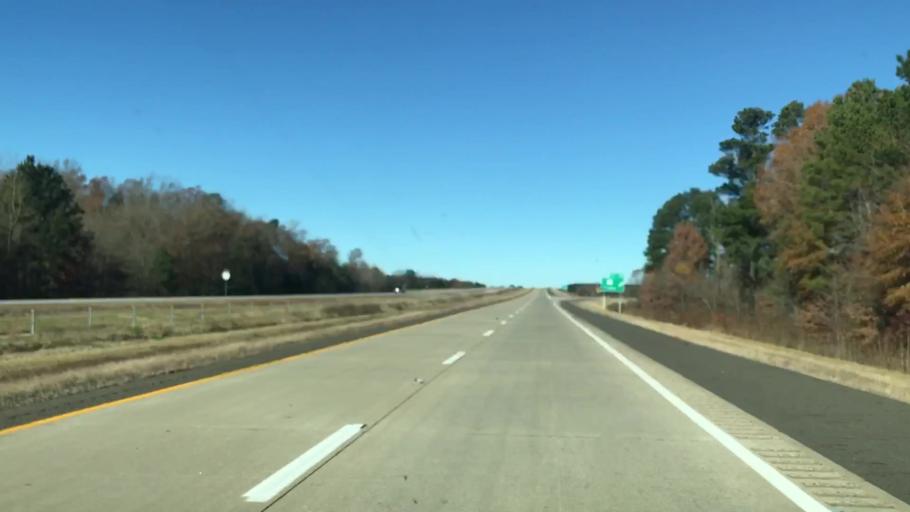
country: US
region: Texas
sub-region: Bowie County
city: Texarkana
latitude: 33.2461
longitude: -93.8785
